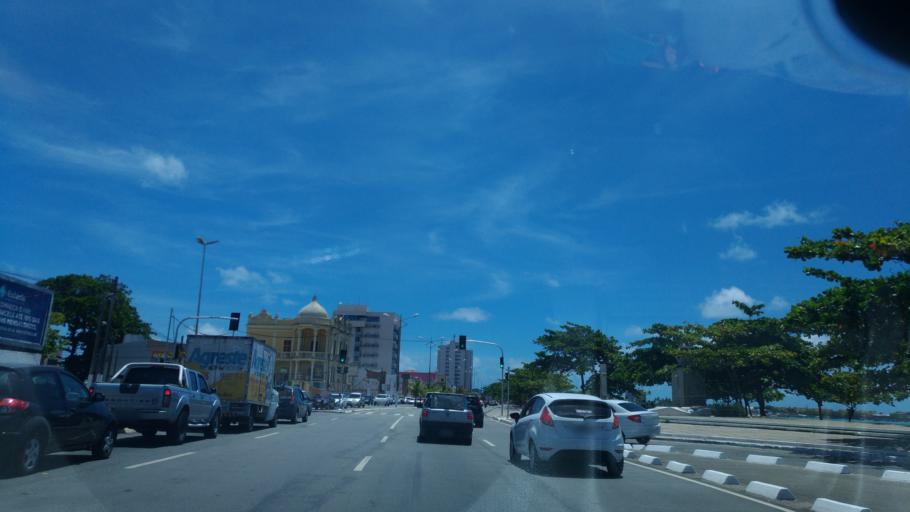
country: BR
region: Alagoas
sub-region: Maceio
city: Maceio
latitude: -9.6696
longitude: -35.7338
